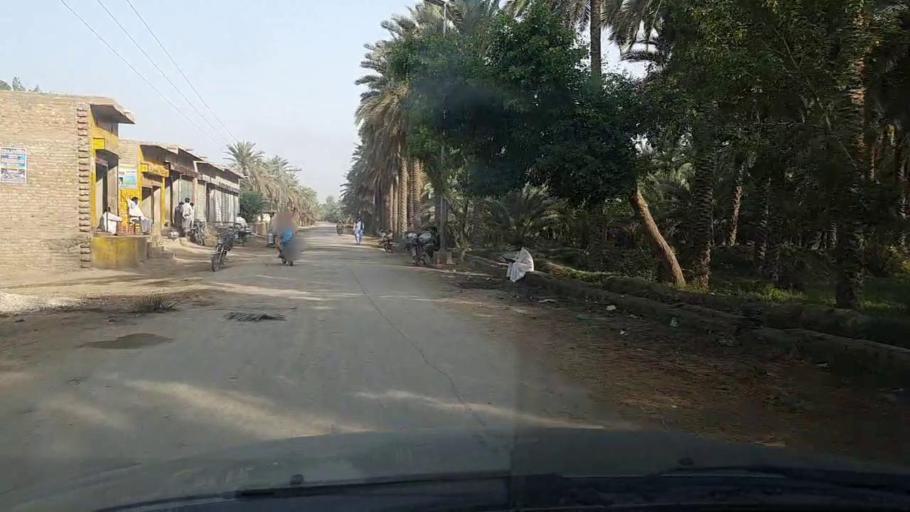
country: PK
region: Sindh
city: Pir jo Goth
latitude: 27.5582
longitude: 68.5558
